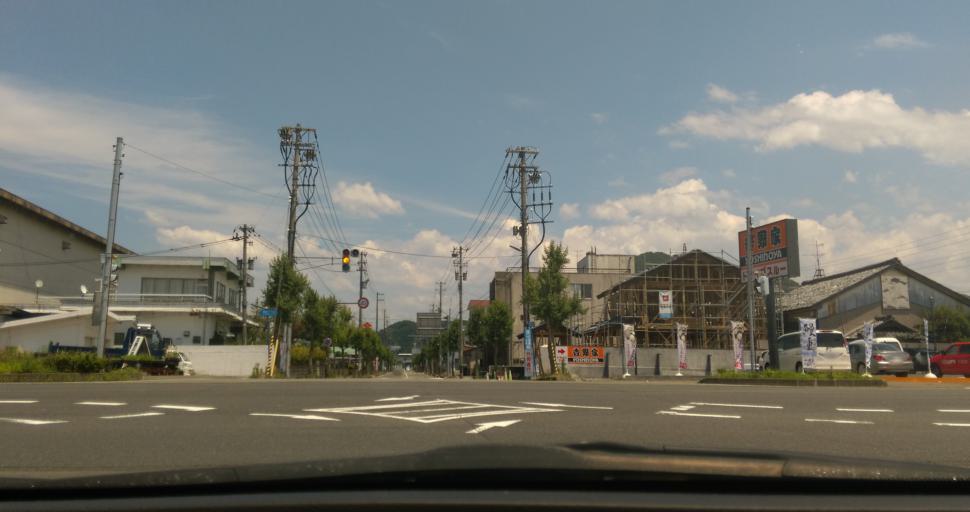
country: JP
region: Fukui
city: Sabae
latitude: 35.9465
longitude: 136.1942
